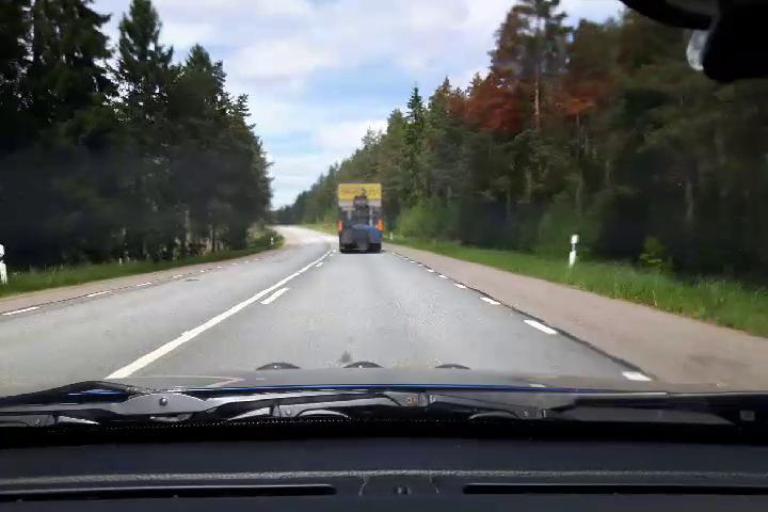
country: SE
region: Uppsala
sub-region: Tierps Kommun
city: Tierp
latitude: 60.2052
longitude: 17.4825
